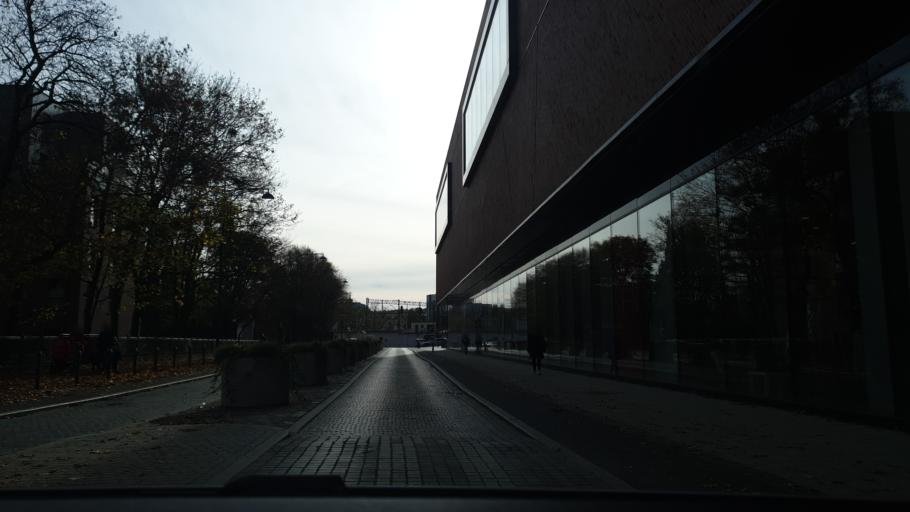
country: PL
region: Pomeranian Voivodeship
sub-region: Gdansk
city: Gdansk
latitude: 54.3830
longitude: 18.6065
